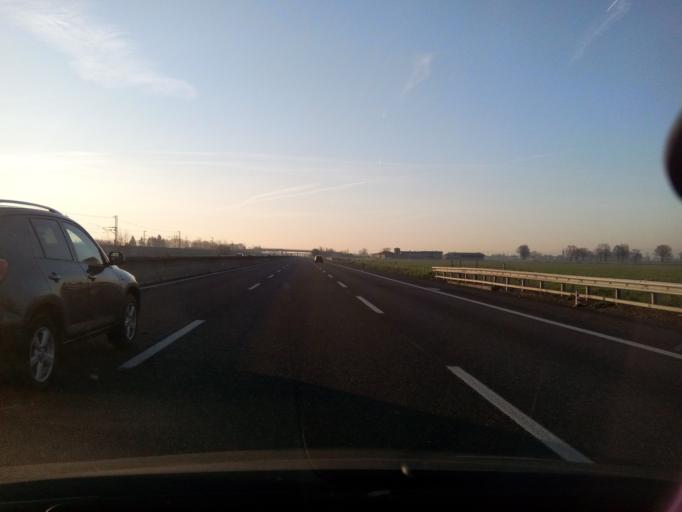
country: IT
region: Lombardy
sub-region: Provincia di Lodi
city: Livraga
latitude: 45.2114
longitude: 9.5350
